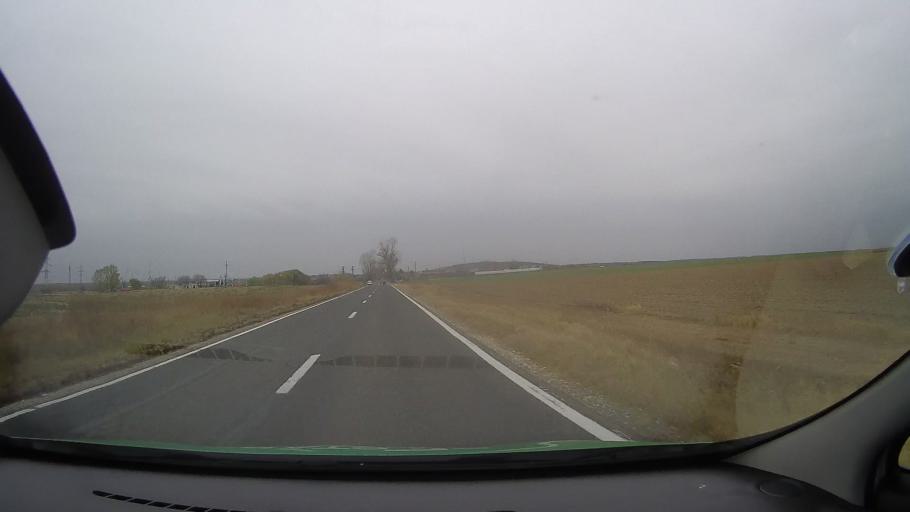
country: RO
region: Constanta
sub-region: Oras Harsova
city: Harsova
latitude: 44.6927
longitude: 27.9722
